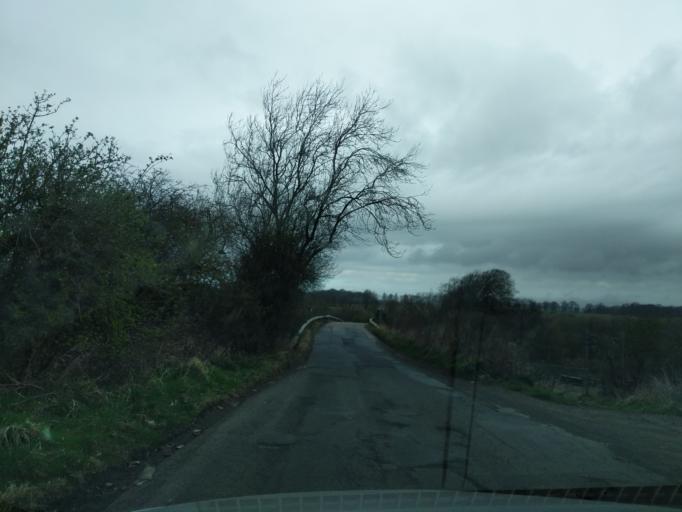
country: GB
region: Scotland
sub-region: Edinburgh
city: Balerno
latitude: 55.8935
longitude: -3.3478
